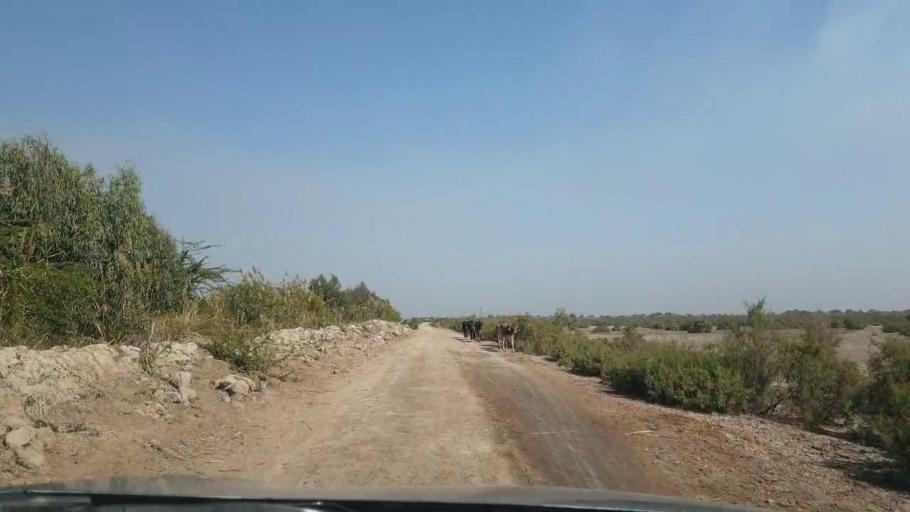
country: PK
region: Sindh
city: Berani
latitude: 25.6534
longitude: 68.8796
